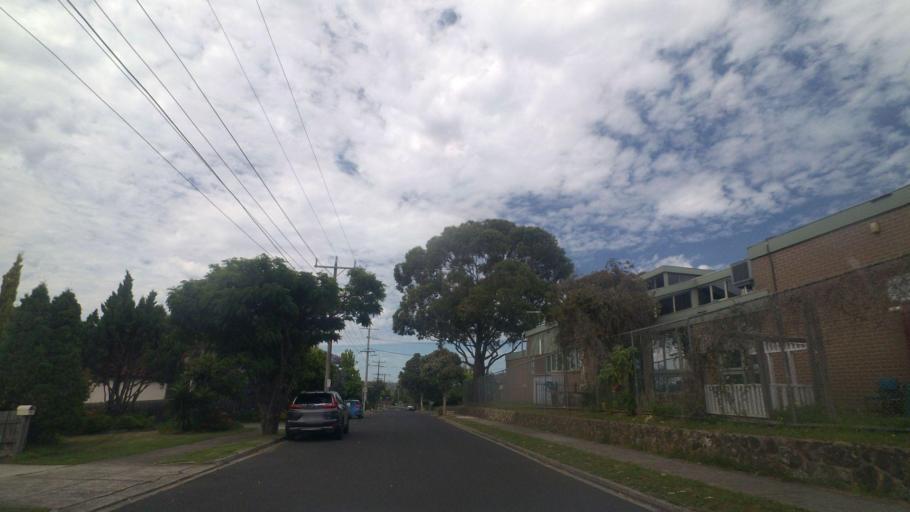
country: AU
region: Victoria
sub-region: Banyule
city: Viewbank
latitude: -37.7346
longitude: 145.0909
